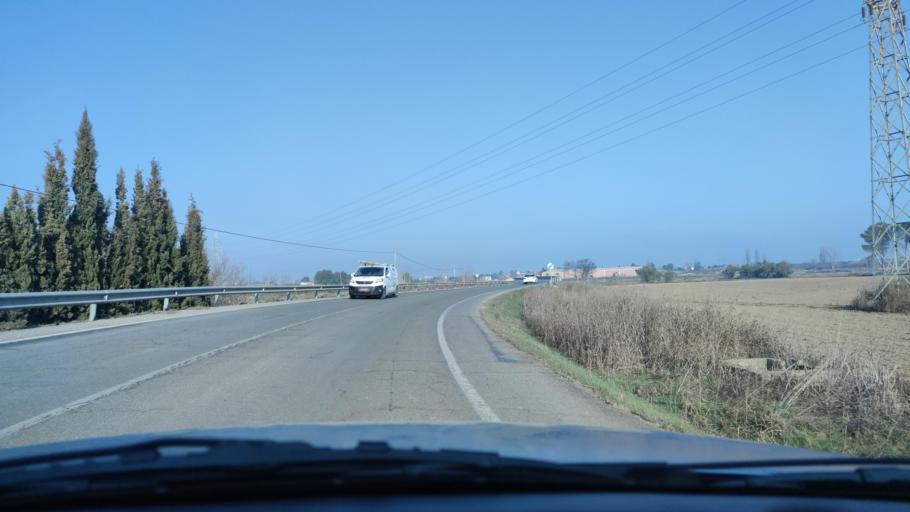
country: ES
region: Catalonia
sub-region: Provincia de Lleida
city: Torrefarrera
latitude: 41.6550
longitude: 0.6333
